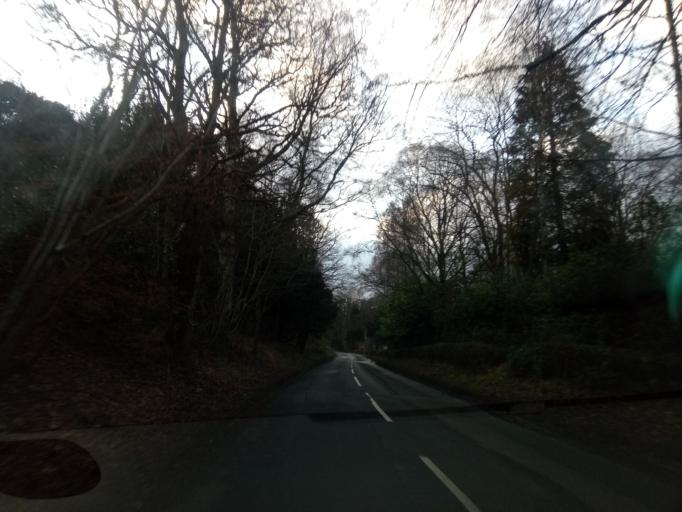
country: GB
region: Scotland
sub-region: The Scottish Borders
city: Galashiels
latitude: 55.5986
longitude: -2.7818
